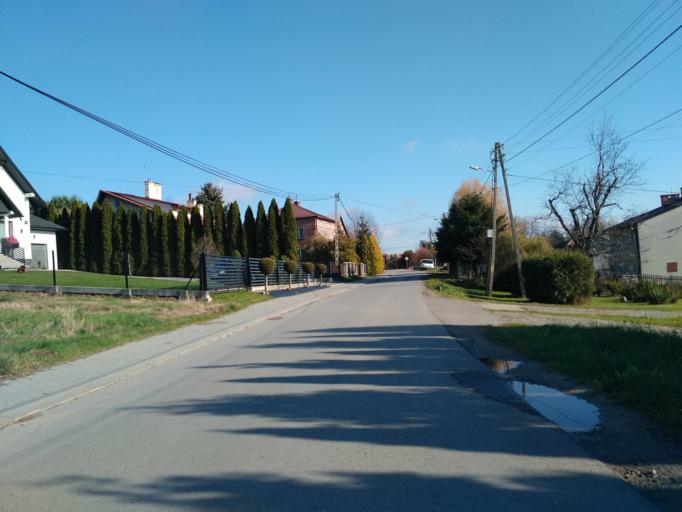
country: PL
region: Subcarpathian Voivodeship
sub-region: Powiat rzeszowski
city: Niechobrz
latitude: 49.9938
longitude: 21.8707
